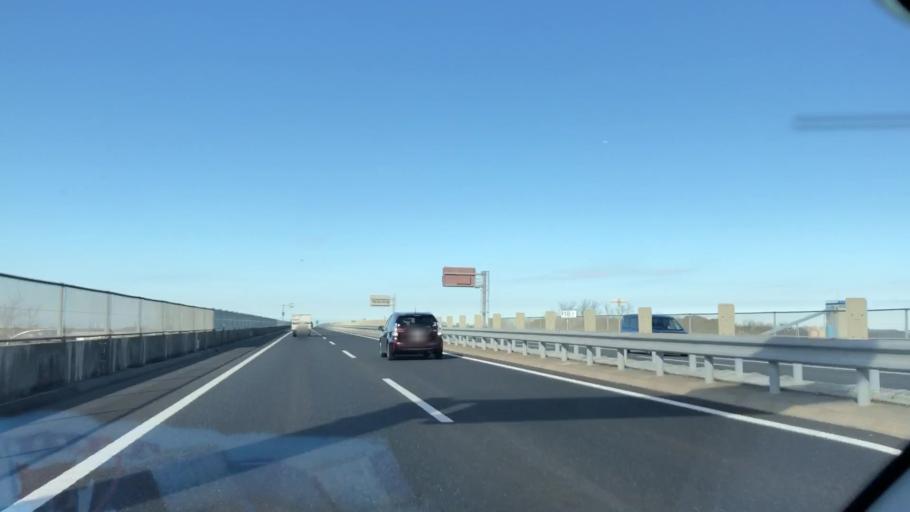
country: JP
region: Chiba
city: Kisarazu
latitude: 35.4169
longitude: 139.9469
